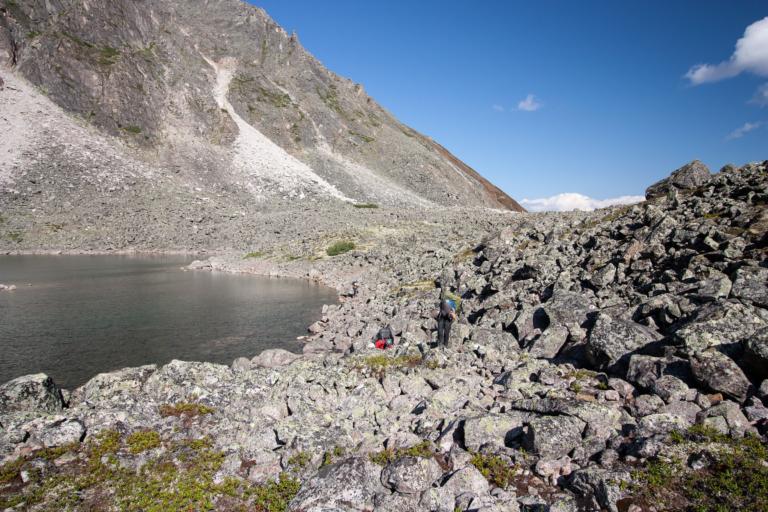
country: RU
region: Respublika Buryatiya
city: Novyy Uoyan
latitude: 56.3027
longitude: 111.2779
